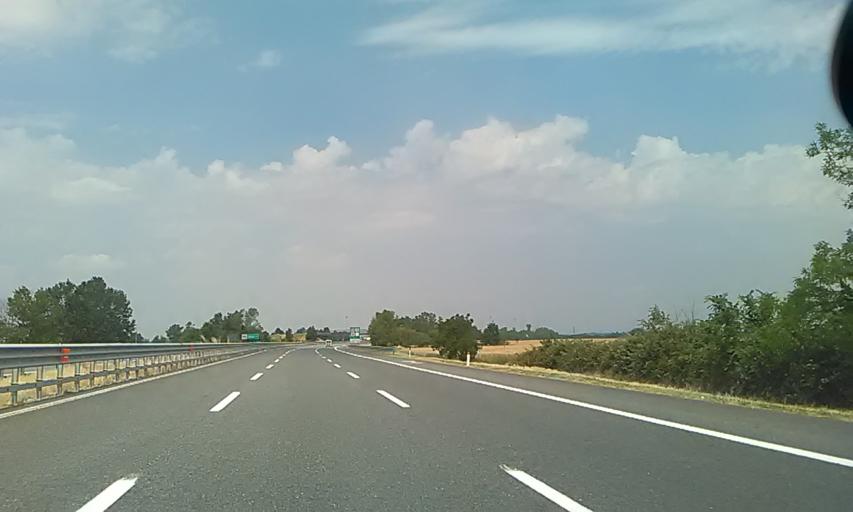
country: IT
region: Piedmont
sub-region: Provincia di Alessandria
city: Castelspina
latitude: 44.8105
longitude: 8.5981
